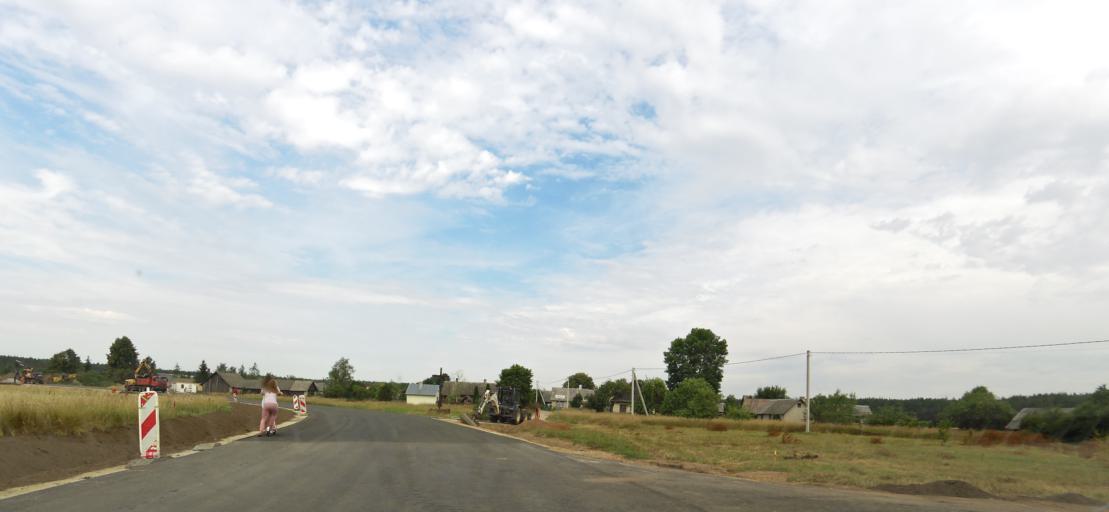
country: LT
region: Vilnius County
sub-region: Trakai
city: Rudiskes
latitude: 54.4629
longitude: 24.9767
